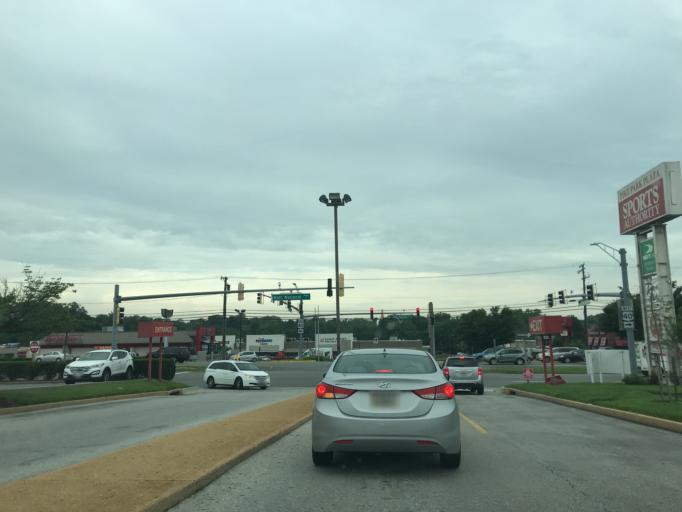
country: US
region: Maryland
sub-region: Baltimore County
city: Catonsville
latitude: 39.2861
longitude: -76.7616
